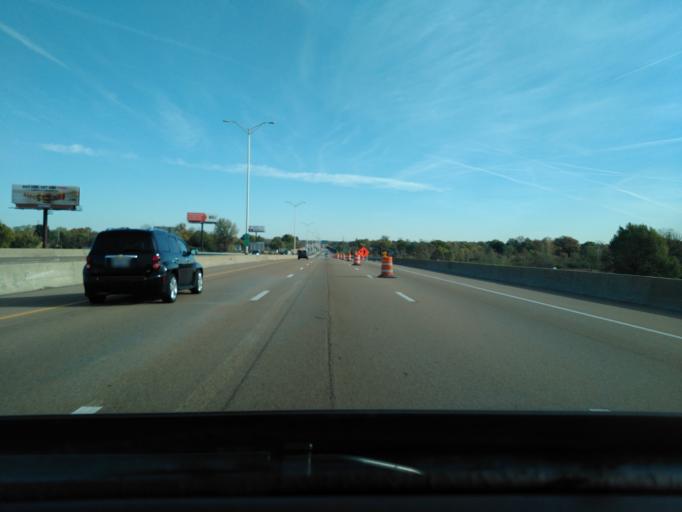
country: US
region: Illinois
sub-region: Saint Clair County
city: Centreville
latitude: 38.5708
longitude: -90.1231
